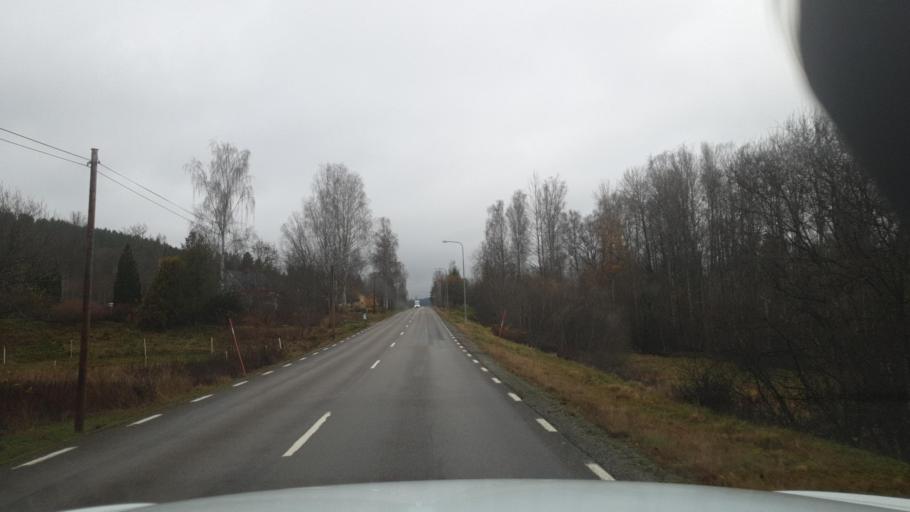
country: SE
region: Vaermland
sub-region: Eda Kommun
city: Amotfors
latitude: 59.6669
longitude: 12.4230
